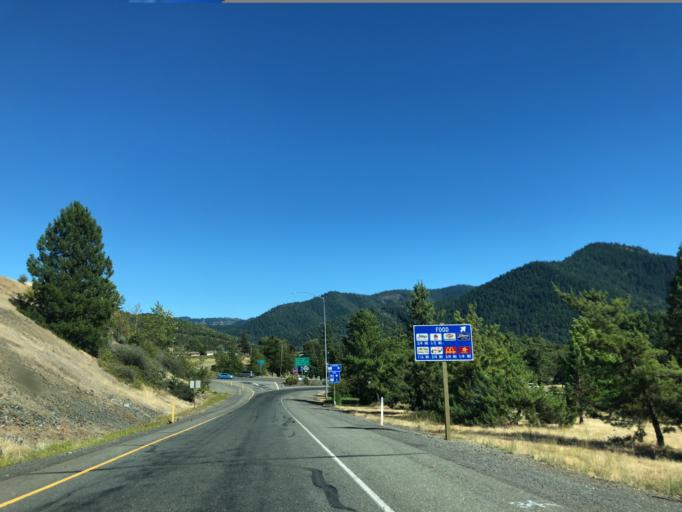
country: US
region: Oregon
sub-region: Josephine County
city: Fruitdale
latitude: 42.4385
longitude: -123.2967
